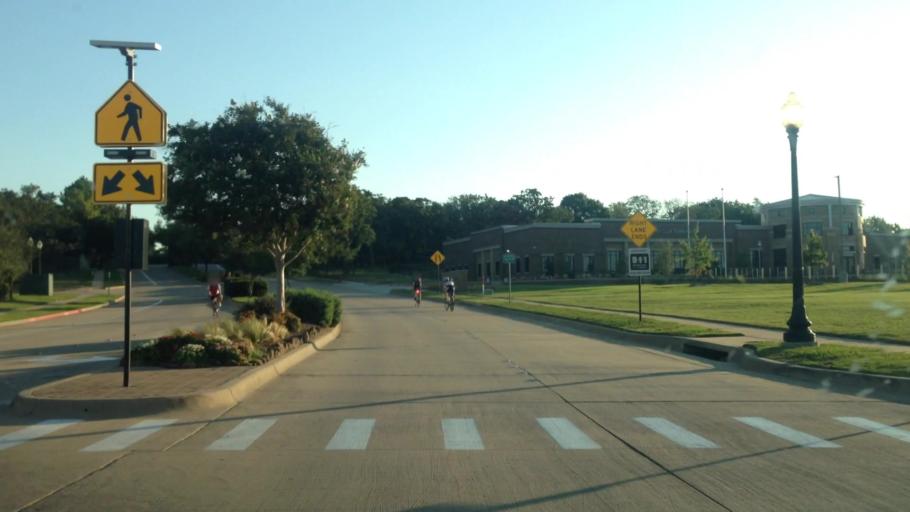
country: US
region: Texas
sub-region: Denton County
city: Trophy Club
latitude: 32.9870
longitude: -97.1705
